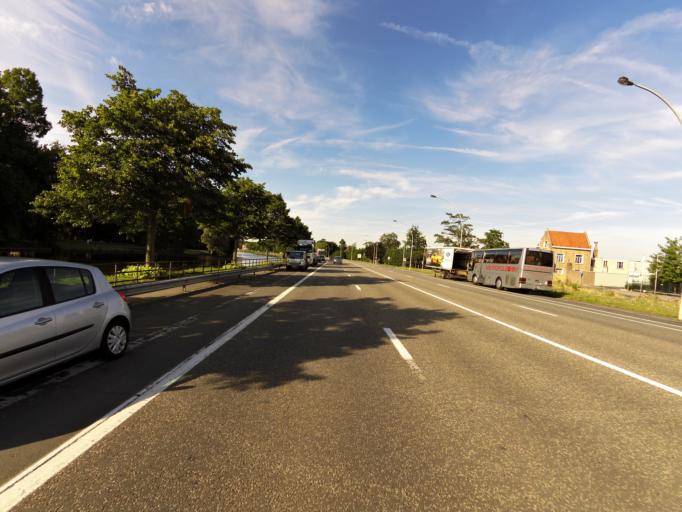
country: BE
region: Flanders
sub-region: Provincie West-Vlaanderen
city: Sint-Kruis
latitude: 51.2068
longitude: 3.2398
